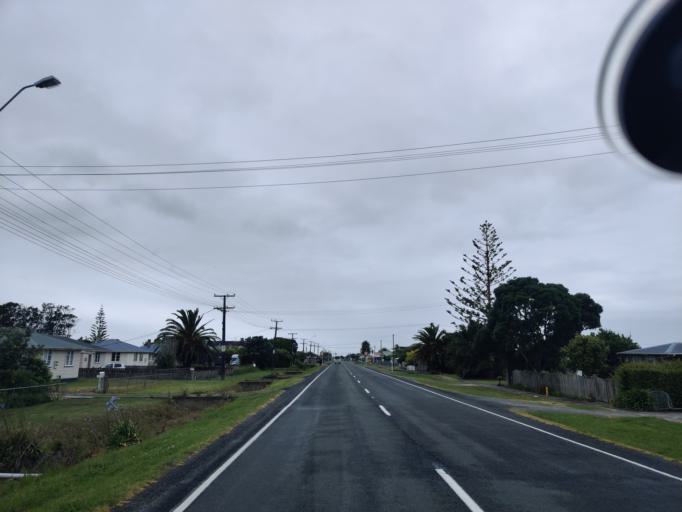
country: NZ
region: Northland
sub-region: Kaipara District
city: Dargaville
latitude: -36.1319
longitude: 174.0201
